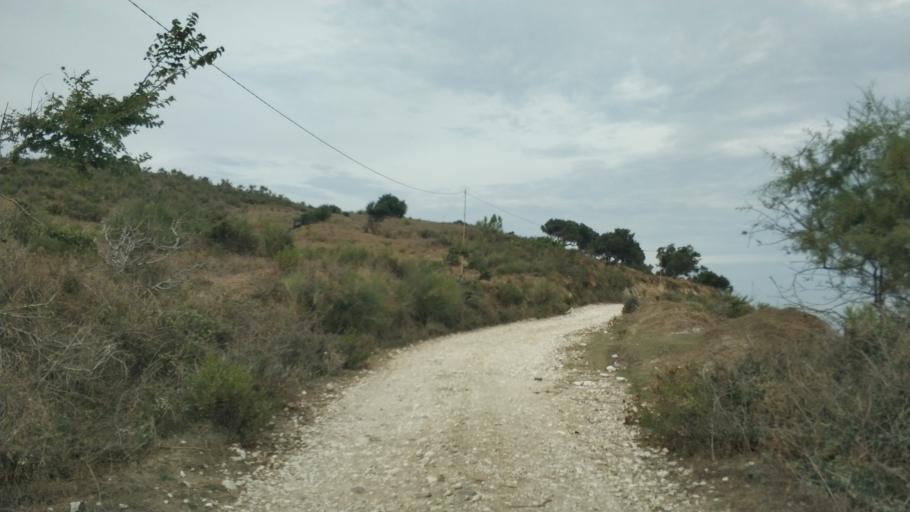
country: AL
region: Vlore
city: Vlore
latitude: 40.5156
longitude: 19.3946
